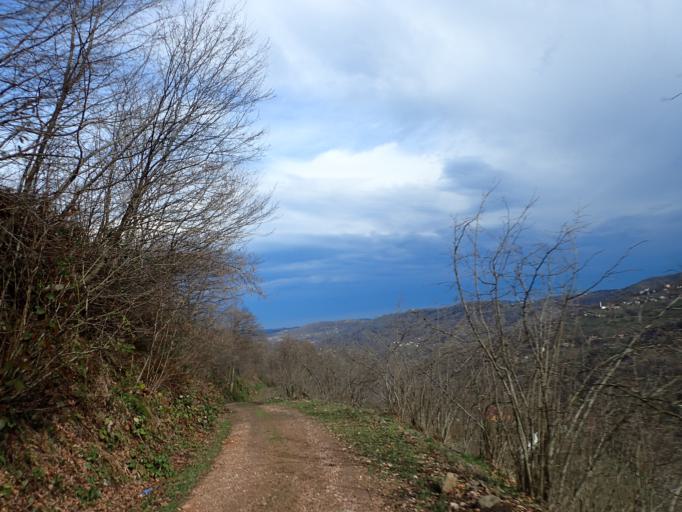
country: TR
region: Ordu
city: Camas
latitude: 40.8881
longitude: 37.5800
